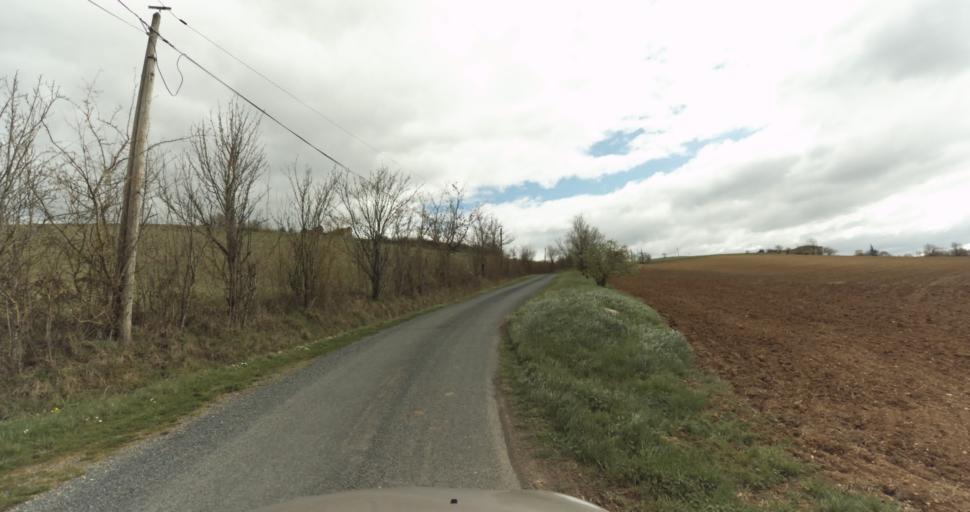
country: FR
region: Midi-Pyrenees
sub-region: Departement du Tarn
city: Puygouzon
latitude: 43.8763
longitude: 2.1648
